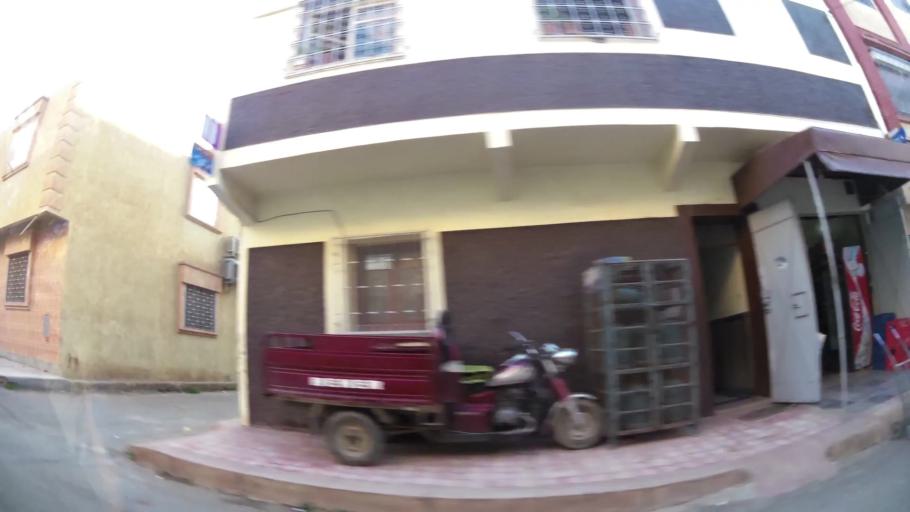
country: MA
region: Oriental
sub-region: Oujda-Angad
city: Oujda
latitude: 34.7078
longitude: -1.9125
